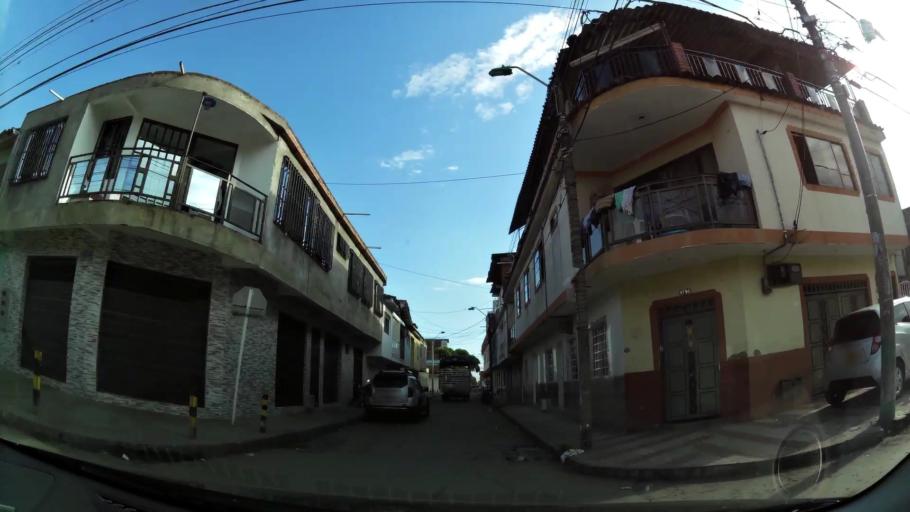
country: CO
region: Valle del Cauca
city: Cali
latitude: 3.4263
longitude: -76.5234
